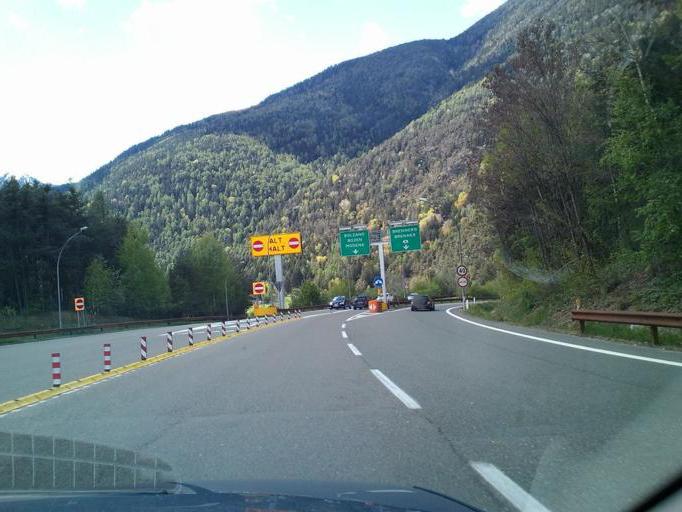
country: IT
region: Trentino-Alto Adige
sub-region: Bolzano
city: Varna
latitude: 46.7636
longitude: 11.6409
